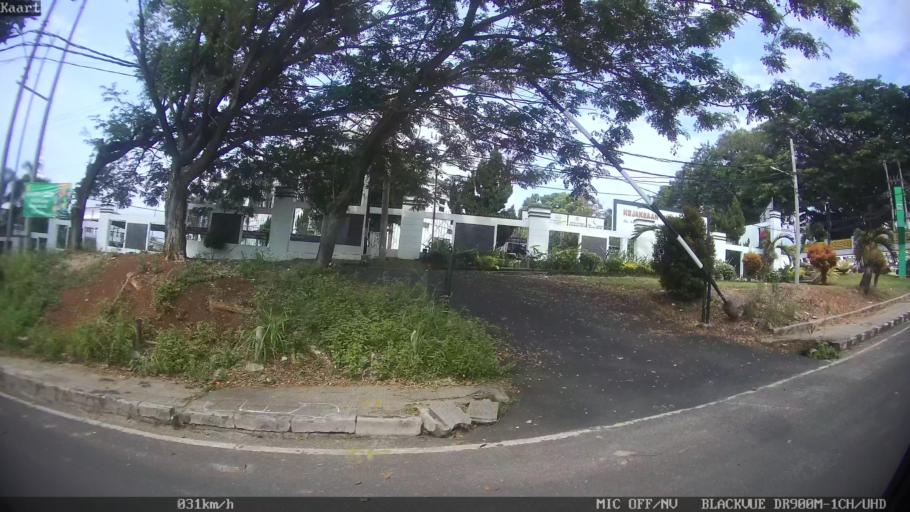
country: ID
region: Lampung
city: Bandarlampung
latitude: -5.4421
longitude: 105.2600
